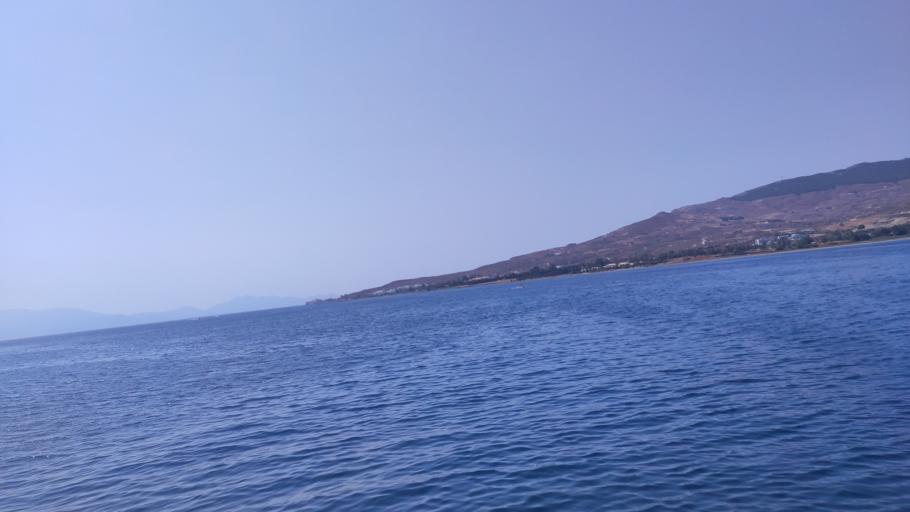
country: GR
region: South Aegean
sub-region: Nomos Dodekanisou
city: Kos
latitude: 36.8931
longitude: 27.3493
